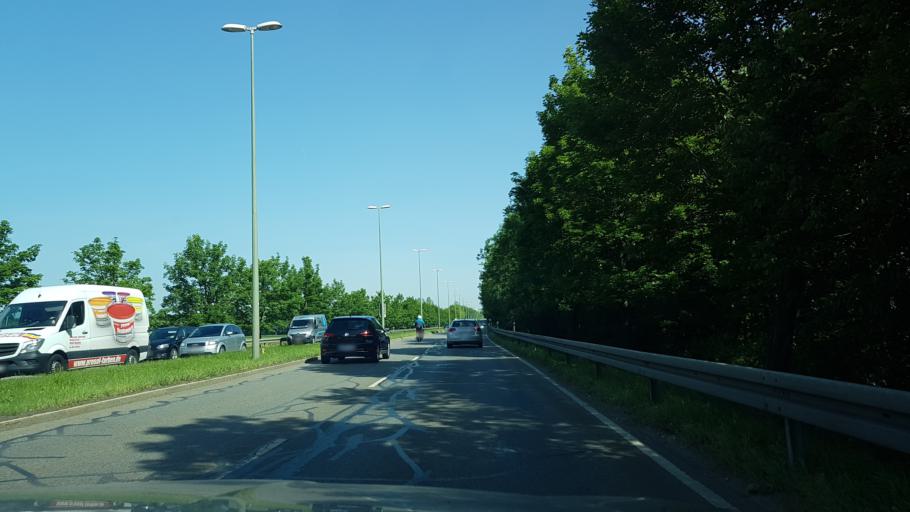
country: DE
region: Bavaria
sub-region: Upper Bavaria
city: Karlsfeld
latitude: 48.2021
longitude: 11.4911
